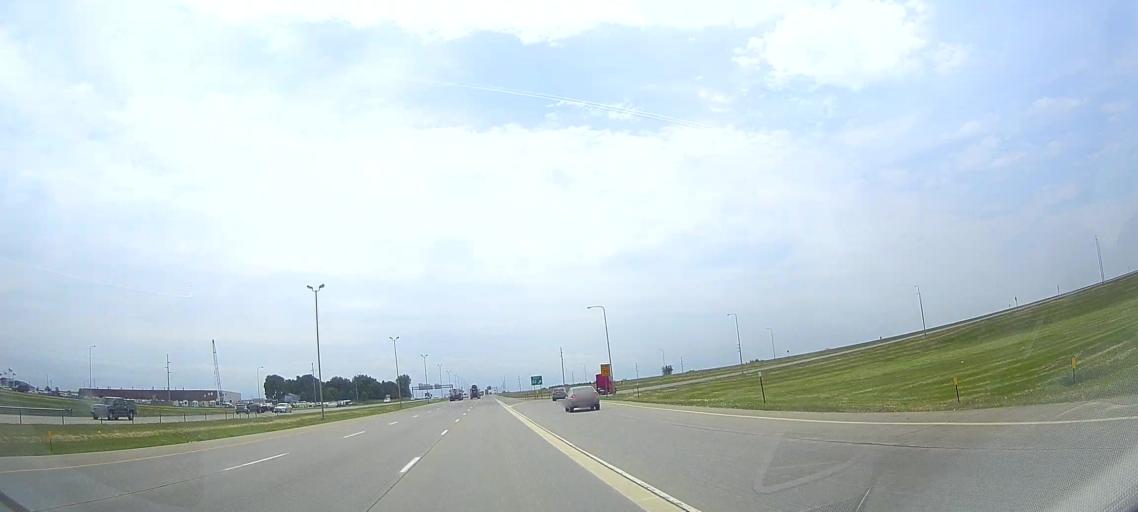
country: US
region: South Dakota
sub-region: Minnehaha County
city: Crooks
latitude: 43.6013
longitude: -96.7713
